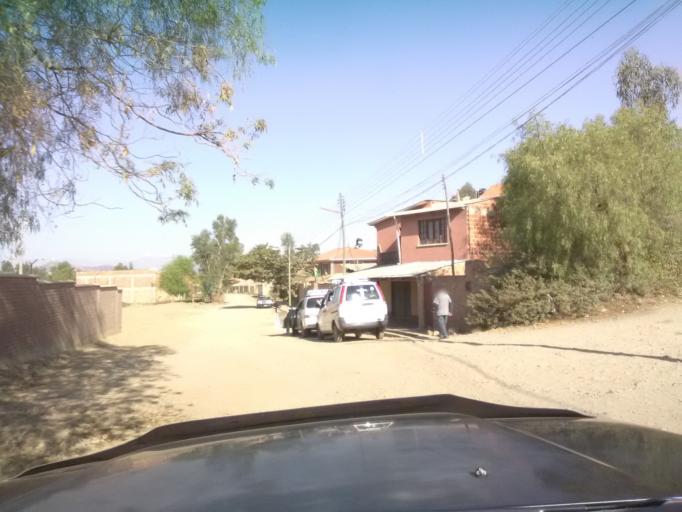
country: BO
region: Cochabamba
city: Cochabamba
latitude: -17.3586
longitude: -66.2026
